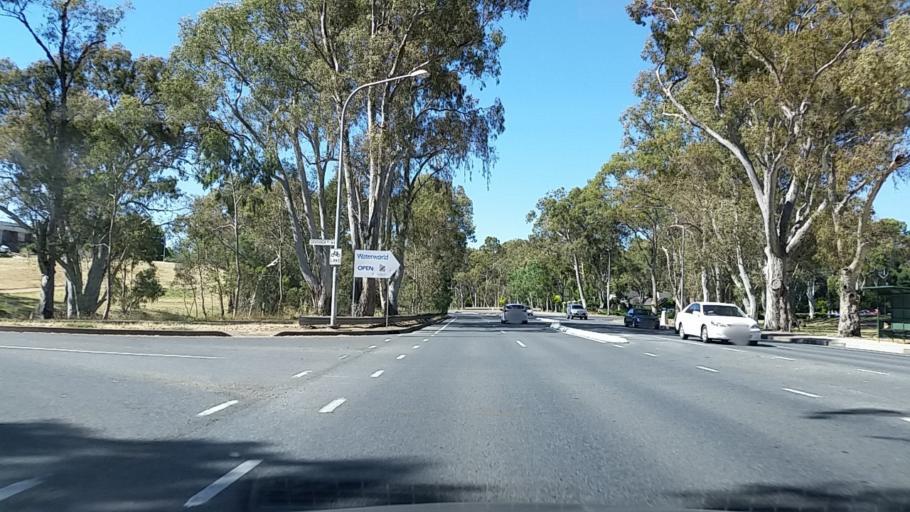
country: AU
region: South Australia
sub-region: Tea Tree Gully
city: Hope Valley
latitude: -34.8217
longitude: 138.6949
